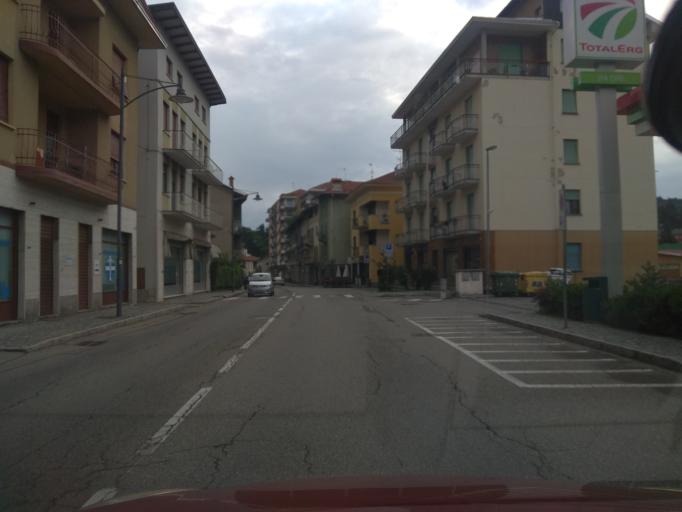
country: IT
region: Piedmont
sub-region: Provincia di Biella
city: Trivero-Prativero-Ponzone
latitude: 45.6540
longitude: 8.1863
